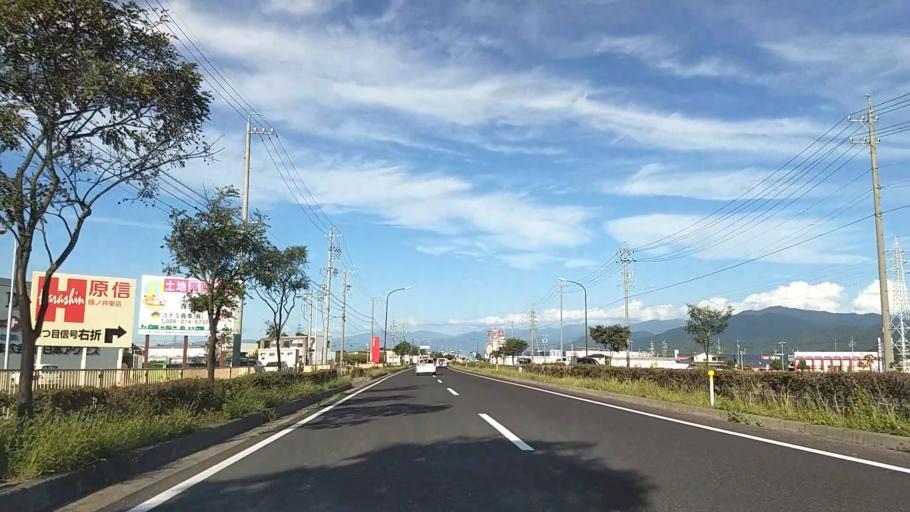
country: JP
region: Nagano
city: Nagano-shi
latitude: 36.5877
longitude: 138.1709
